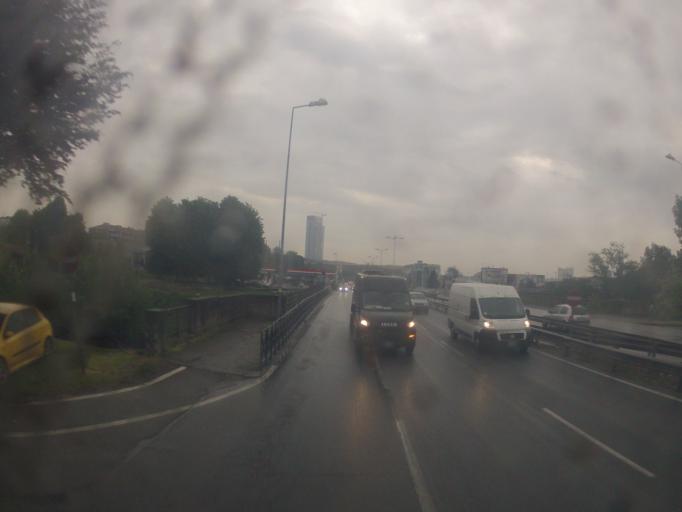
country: IT
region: Piedmont
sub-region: Provincia di Torino
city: Moncalieri
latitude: 45.0130
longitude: 7.6696
